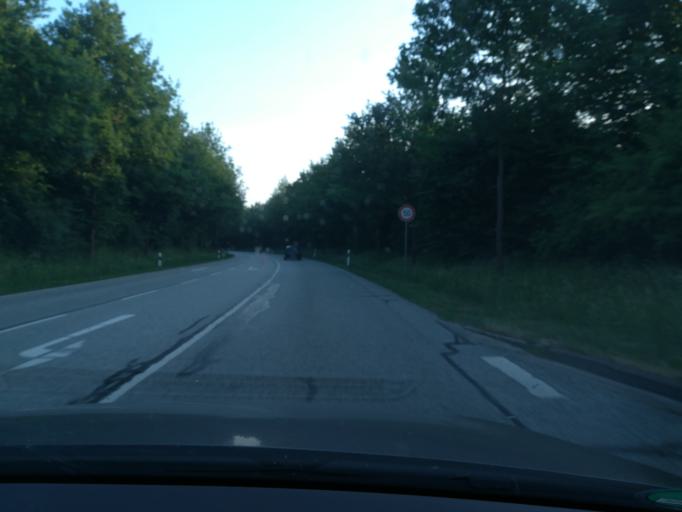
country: DE
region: Schleswig-Holstein
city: Schwarzenbek
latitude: 53.5127
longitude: 10.4767
